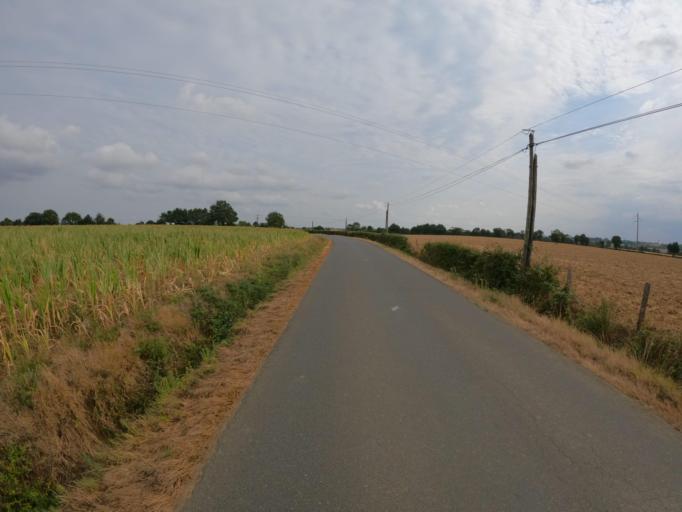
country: FR
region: Pays de la Loire
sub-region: Departement de Maine-et-Loire
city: Saint-Christophe-du-Bois
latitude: 47.0319
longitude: -0.9576
